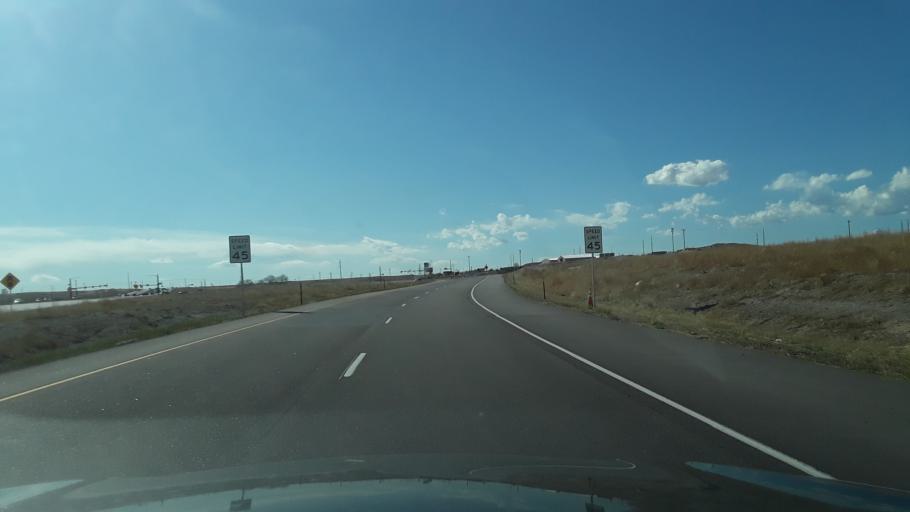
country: US
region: Colorado
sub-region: Pueblo County
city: Pueblo
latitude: 38.3136
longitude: -104.6556
